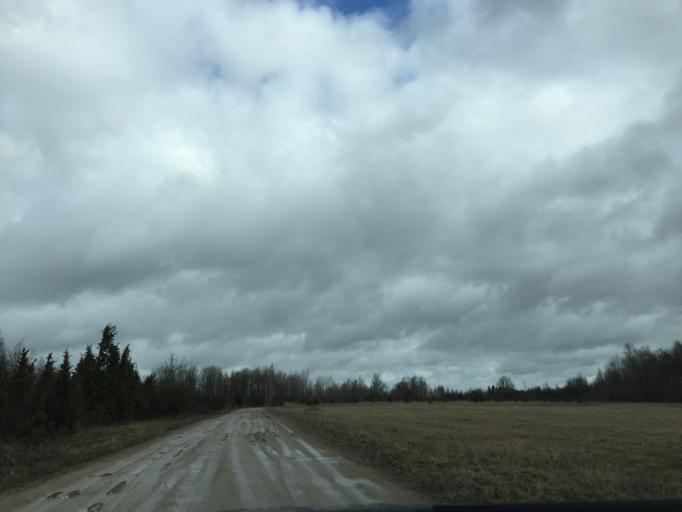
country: EE
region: Laeaene
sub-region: Haapsalu linn
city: Haapsalu
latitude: 58.6823
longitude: 23.5420
